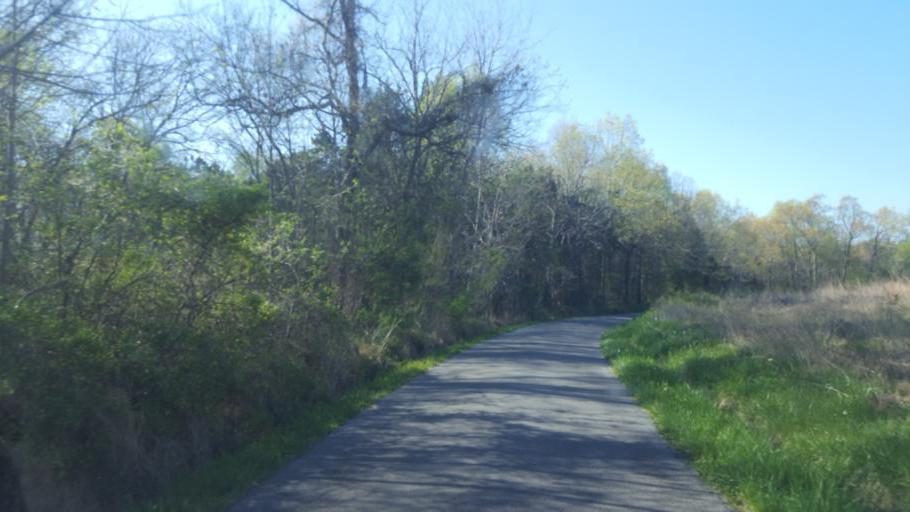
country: US
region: Kentucky
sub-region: Barren County
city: Cave City
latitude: 37.1777
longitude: -86.0477
